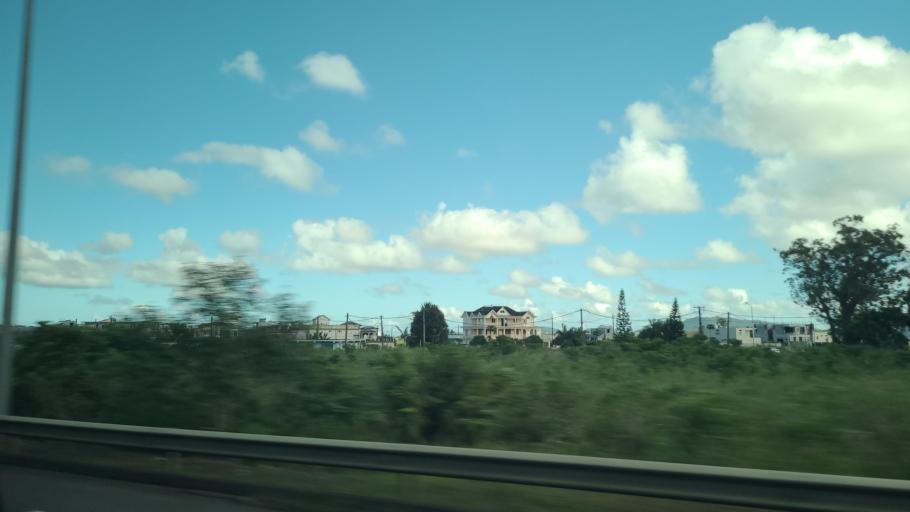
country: MU
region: Moka
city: Providence
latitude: -20.2461
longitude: 57.6064
